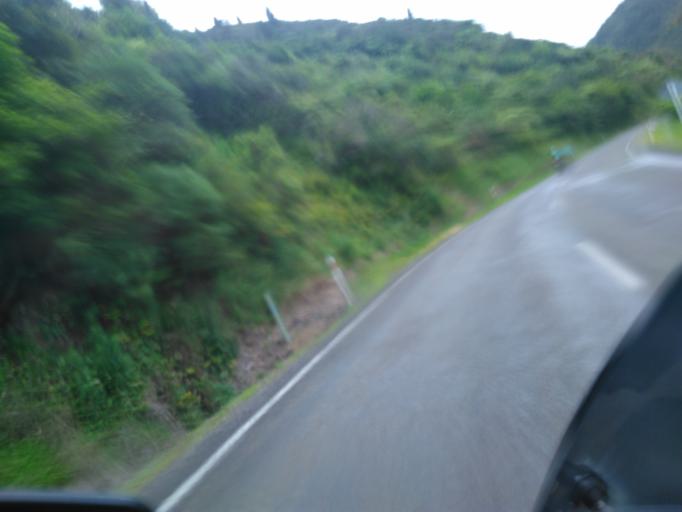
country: NZ
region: Bay of Plenty
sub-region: Opotiki District
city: Opotiki
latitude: -38.2423
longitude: 177.3113
